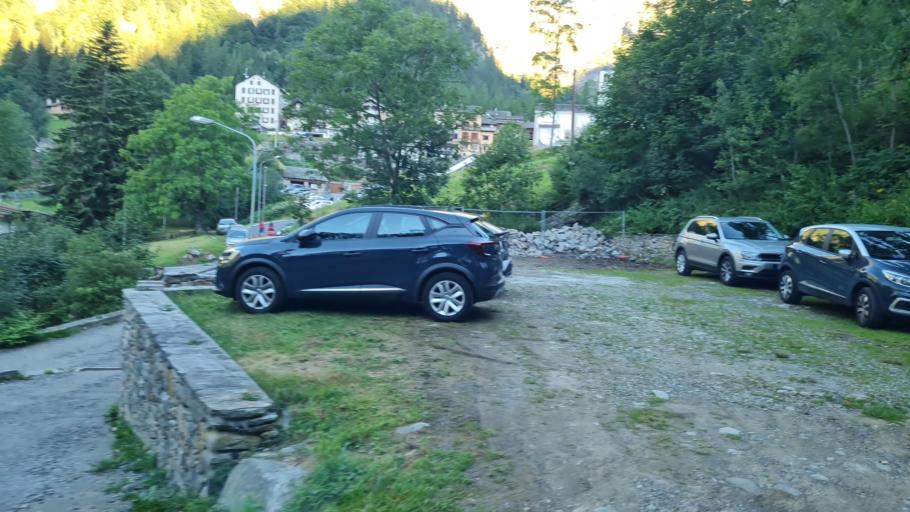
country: IT
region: Piedmont
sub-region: Provincia di Vercelli
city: Rima
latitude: 45.8845
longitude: 8.0018
